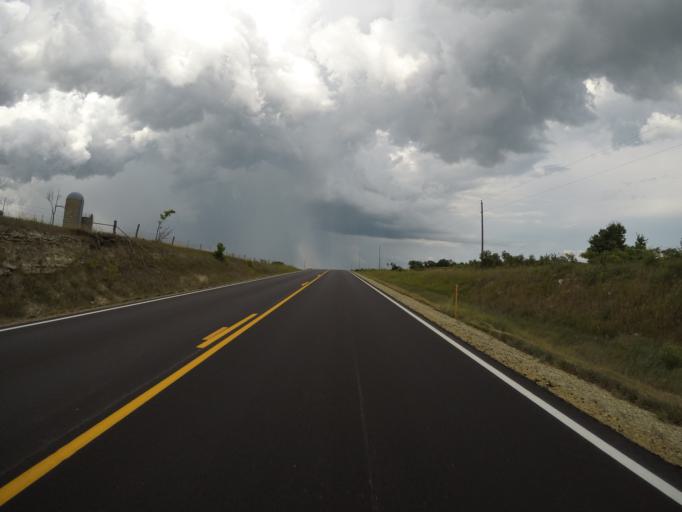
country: US
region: Kansas
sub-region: Marshall County
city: Blue Rapids
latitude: 39.4367
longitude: -96.8258
